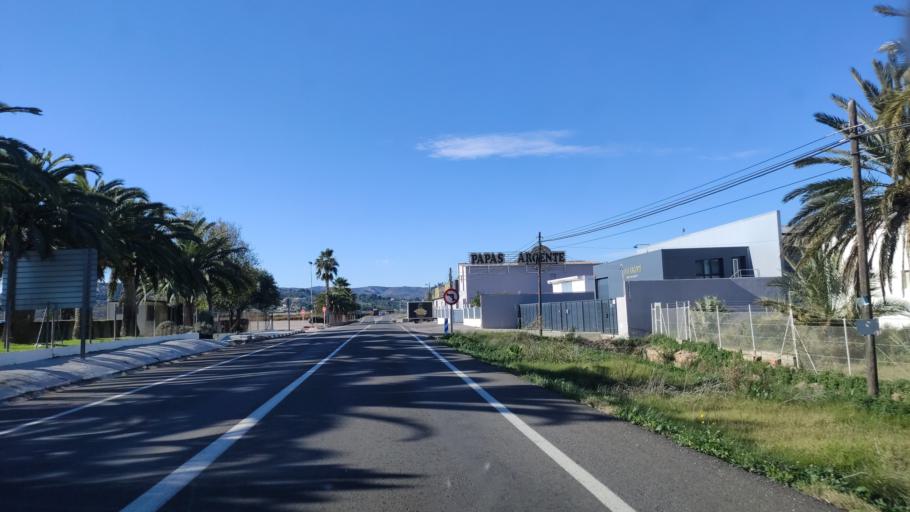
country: ES
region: Valencia
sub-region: Provincia de Valencia
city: Alberic
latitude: 39.1197
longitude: -0.5342
